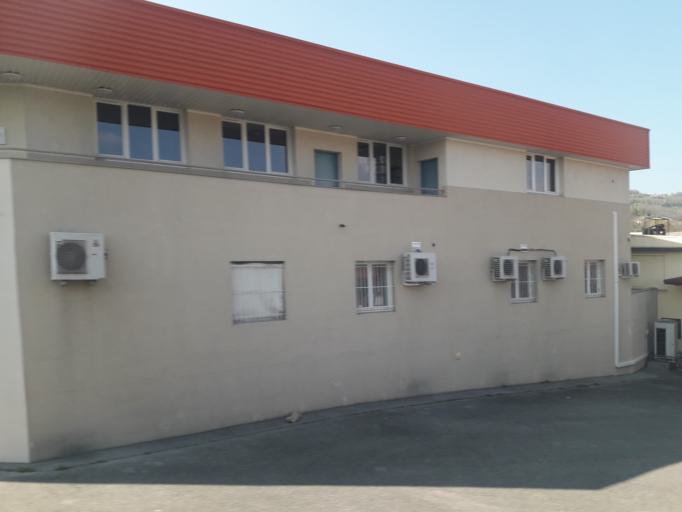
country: FR
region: Rhone-Alpes
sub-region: Departement de l'Isere
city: Saint-Marcellin
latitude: 45.1457
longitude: 5.3105
